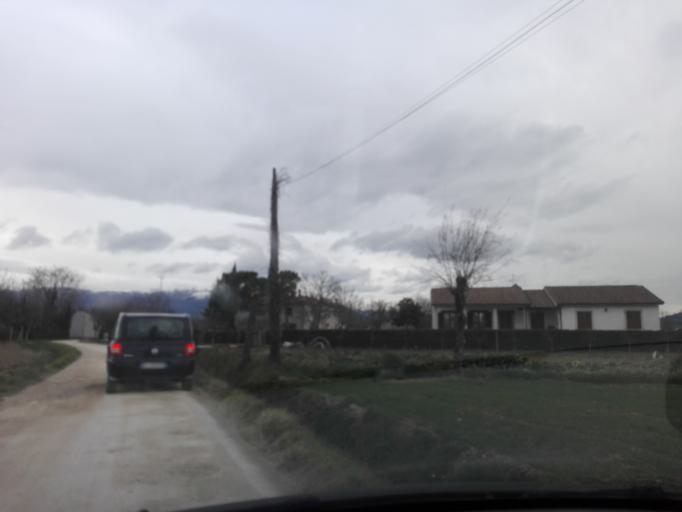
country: IT
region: Umbria
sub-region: Provincia di Perugia
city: Bevagna
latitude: 42.9464
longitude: 12.6481
